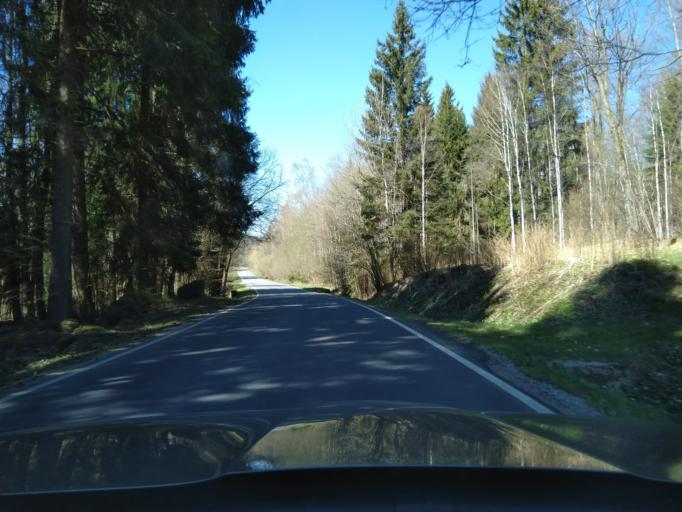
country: CZ
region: Jihocesky
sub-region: Okres Prachatice
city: Vimperk
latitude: 48.9551
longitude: 13.7736
